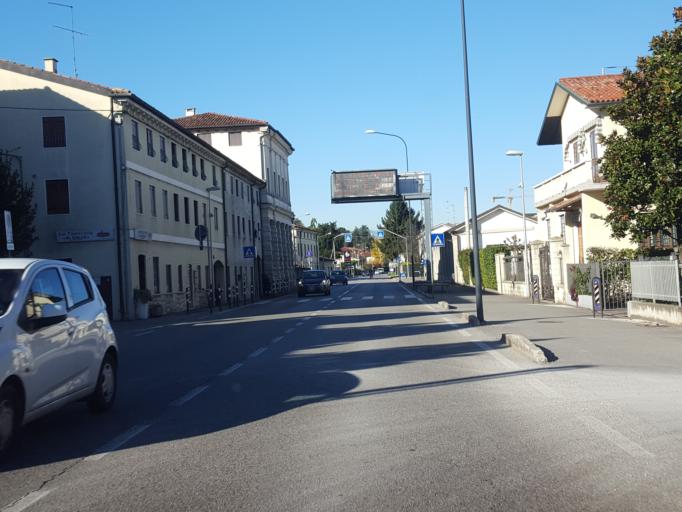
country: IT
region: Veneto
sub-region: Provincia di Vicenza
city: Vicenza
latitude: 45.5338
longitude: 11.5607
